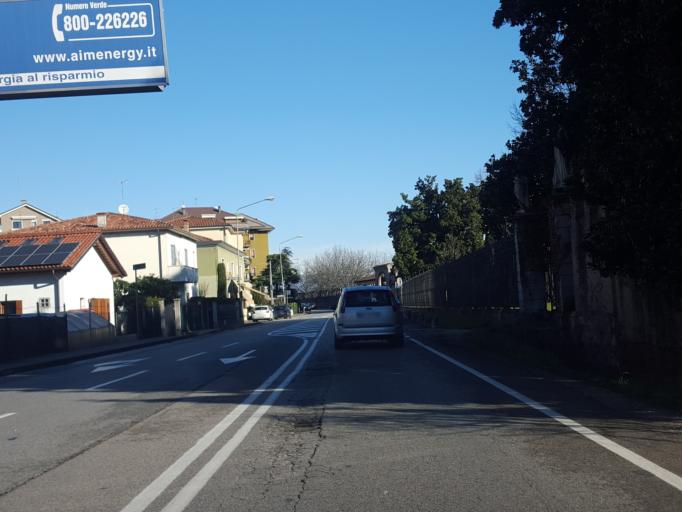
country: IT
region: Veneto
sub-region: Provincia di Vicenza
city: Vicenza
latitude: 45.5654
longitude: 11.5467
